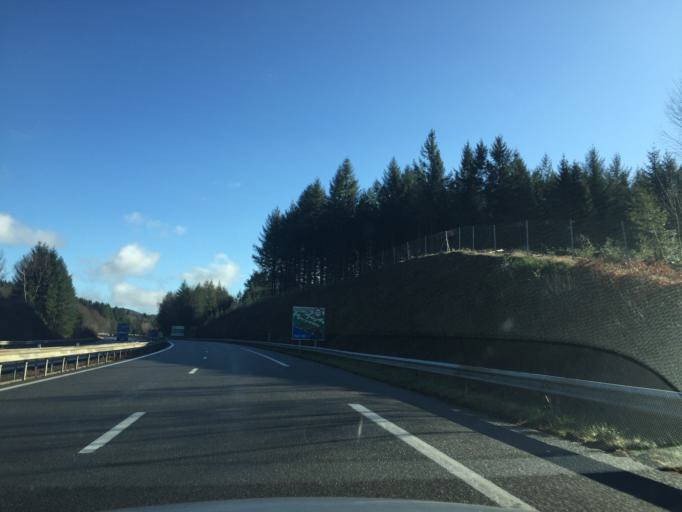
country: FR
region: Auvergne
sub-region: Departement du Puy-de-Dome
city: Celles-sur-Durolle
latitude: 45.8786
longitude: 3.6315
